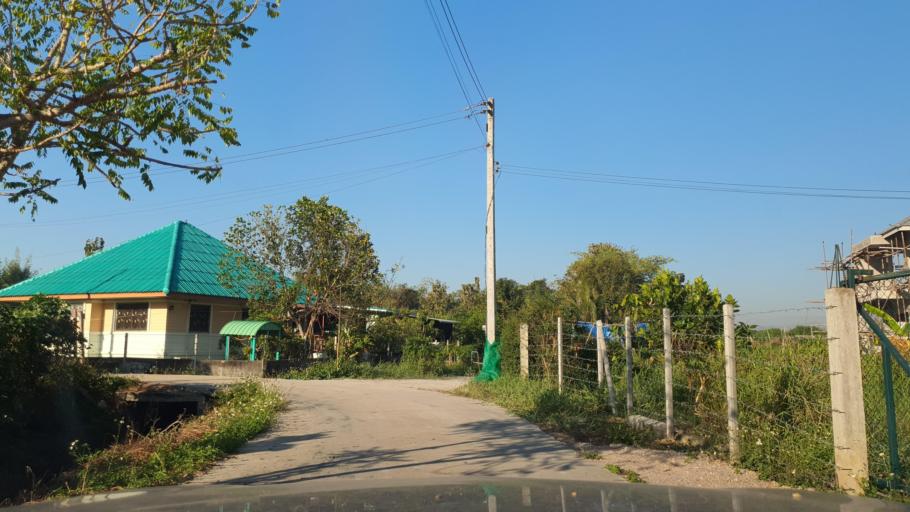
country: TH
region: Chiang Mai
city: Hang Dong
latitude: 18.6937
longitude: 98.9651
